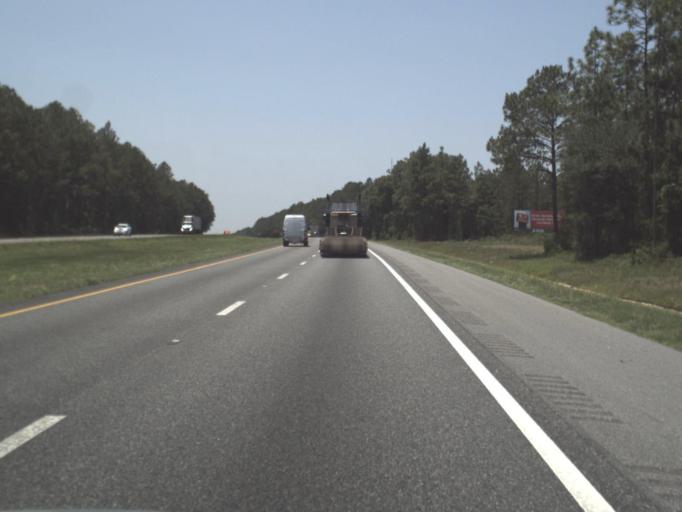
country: US
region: Florida
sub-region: Baker County
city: Macclenny
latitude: 30.2784
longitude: -82.0675
